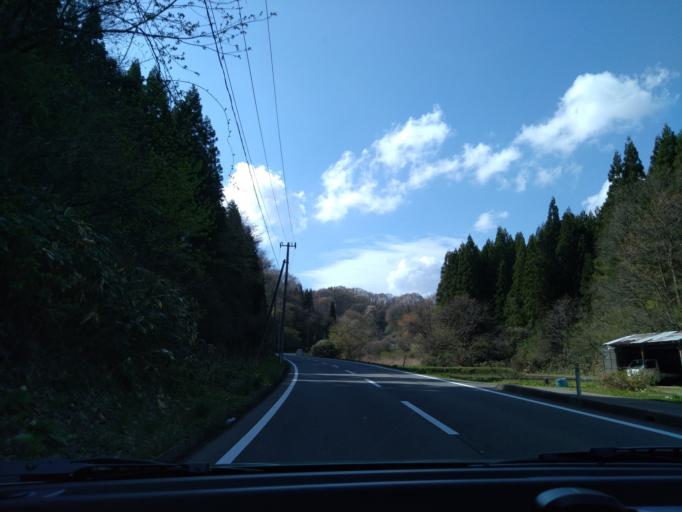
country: JP
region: Akita
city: Akita
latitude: 39.6917
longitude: 140.2245
